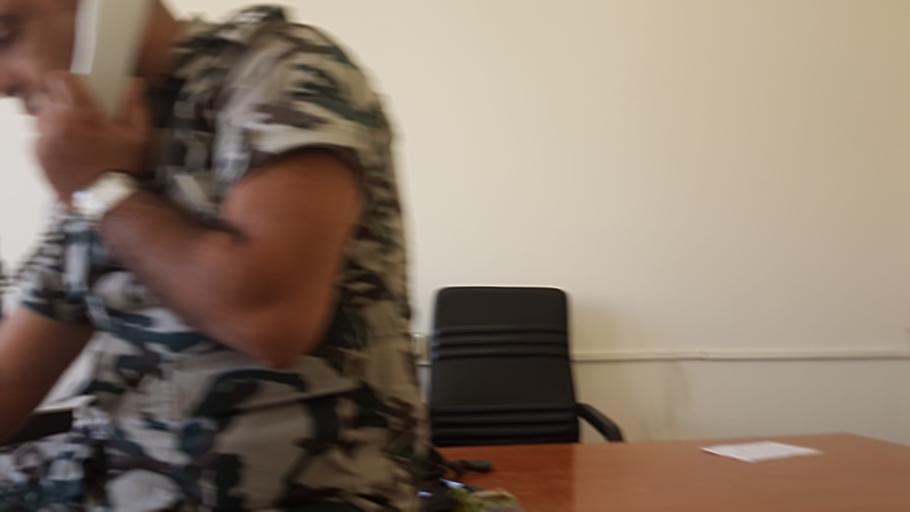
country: LB
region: Beyrouth
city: Beirut
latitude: 33.8790
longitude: 35.5188
